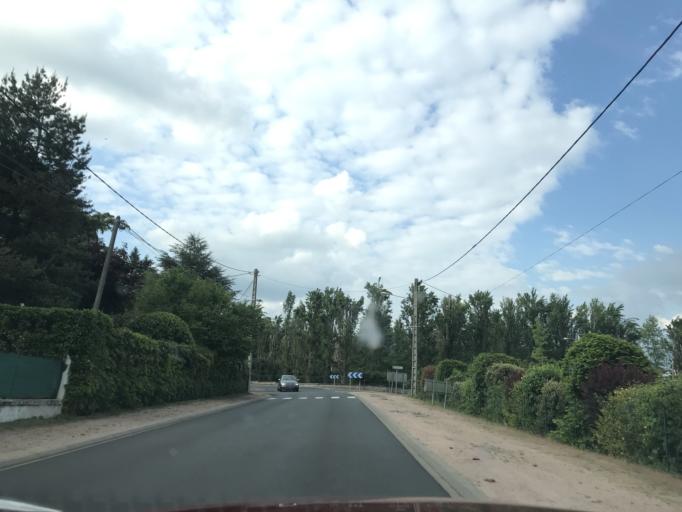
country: FR
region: Auvergne
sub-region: Departement du Puy-de-Dome
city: Lezoux
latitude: 45.8431
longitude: 3.3923
